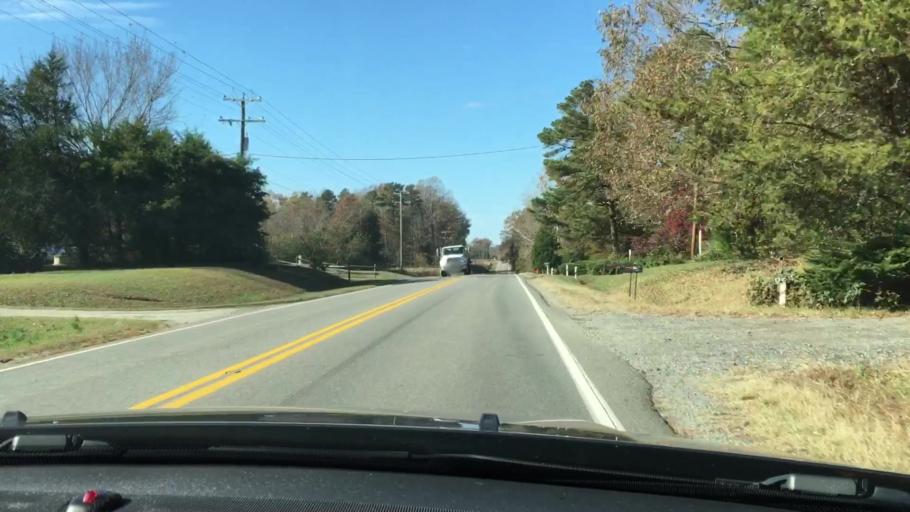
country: US
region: Virginia
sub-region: King William County
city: King William
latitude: 37.7054
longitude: -77.0497
